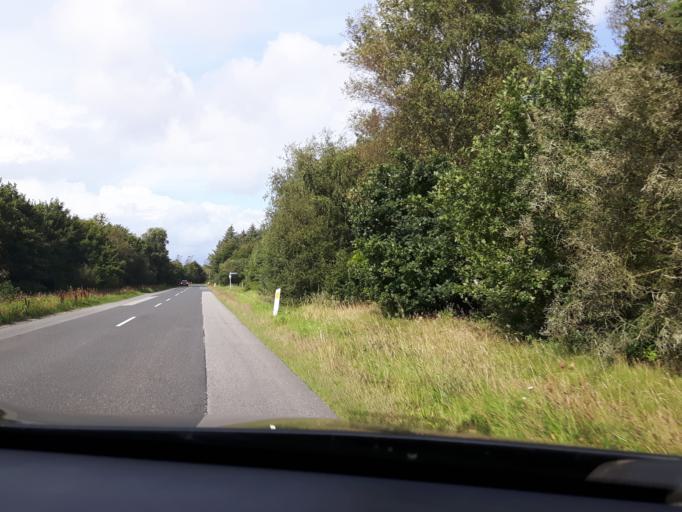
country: DK
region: North Denmark
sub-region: Jammerbugt Kommune
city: Kas
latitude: 57.1873
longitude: 9.5916
